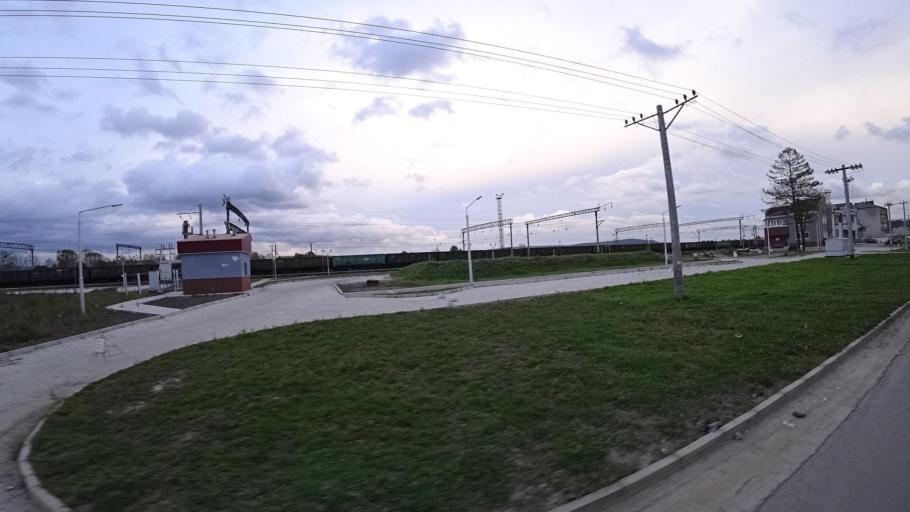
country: RU
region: Jewish Autonomous Oblast
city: Izvestkovyy
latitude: 48.9836
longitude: 131.5548
